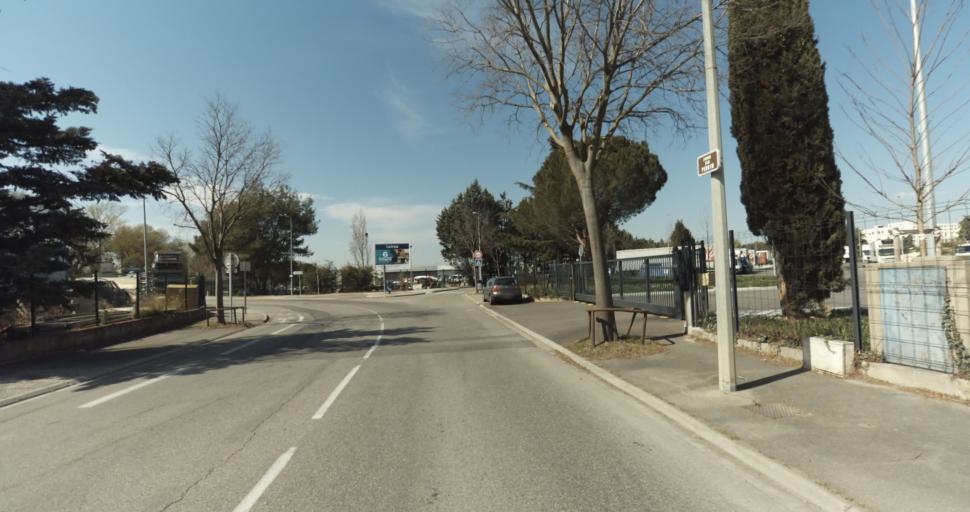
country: FR
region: Provence-Alpes-Cote d'Azur
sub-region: Departement des Bouches-du-Rhone
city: Cabries
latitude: 43.4881
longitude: 5.3710
